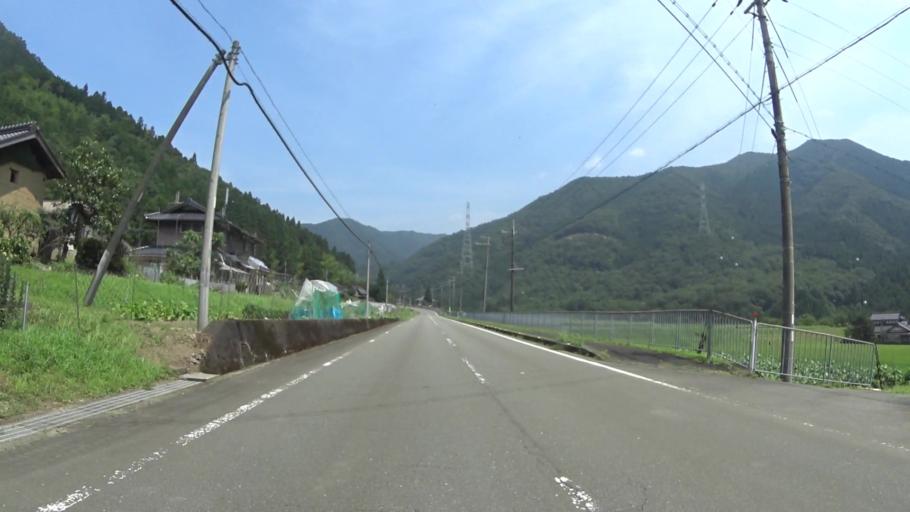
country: JP
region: Kyoto
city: Ayabe
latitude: 35.2707
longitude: 135.4309
